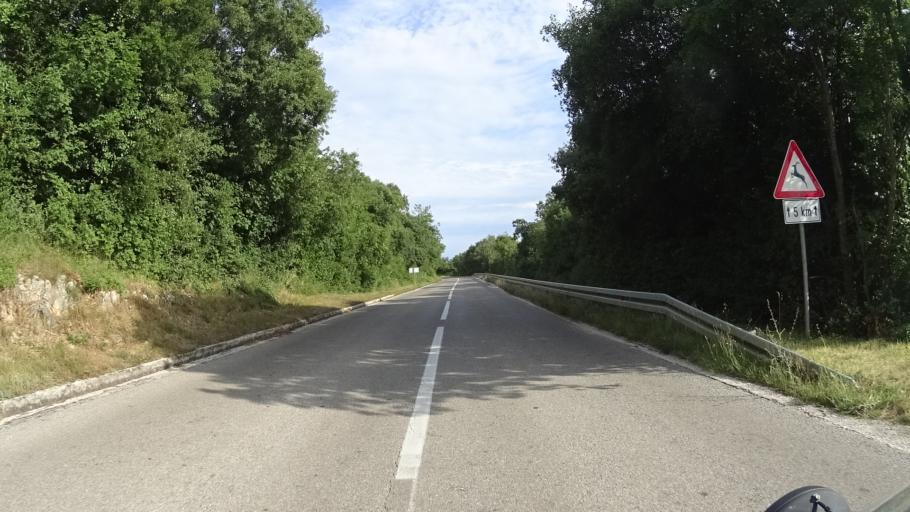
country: HR
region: Istarska
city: Rasa
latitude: 45.0225
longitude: 14.0877
